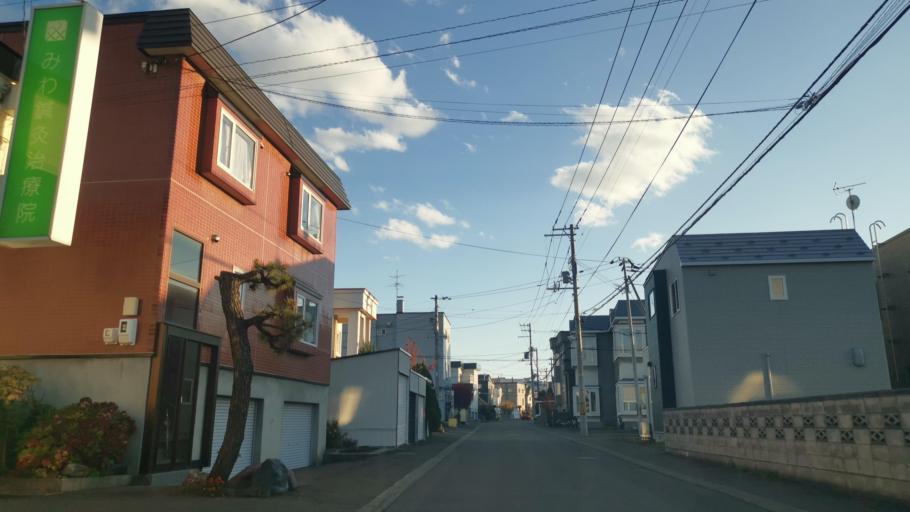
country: JP
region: Hokkaido
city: Sapporo
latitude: 43.0041
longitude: 141.3664
